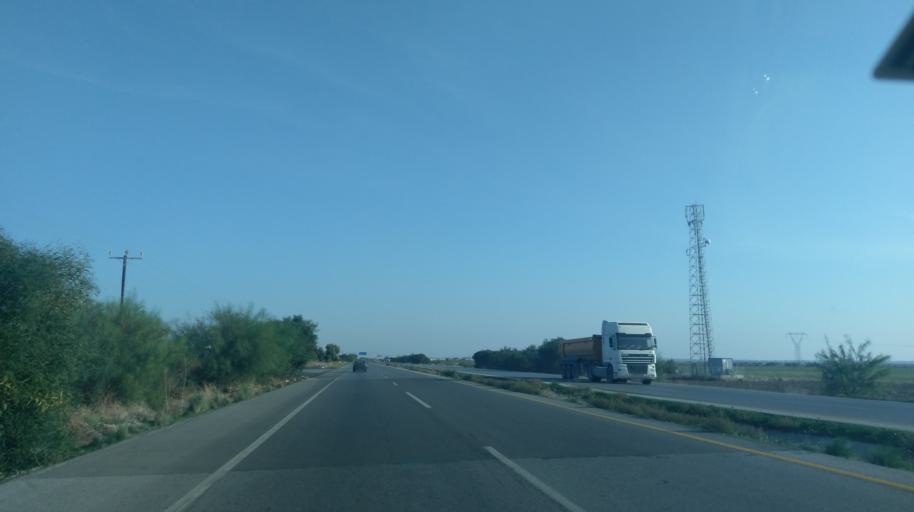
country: CY
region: Ammochostos
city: Acheritou
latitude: 35.1585
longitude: 33.8376
